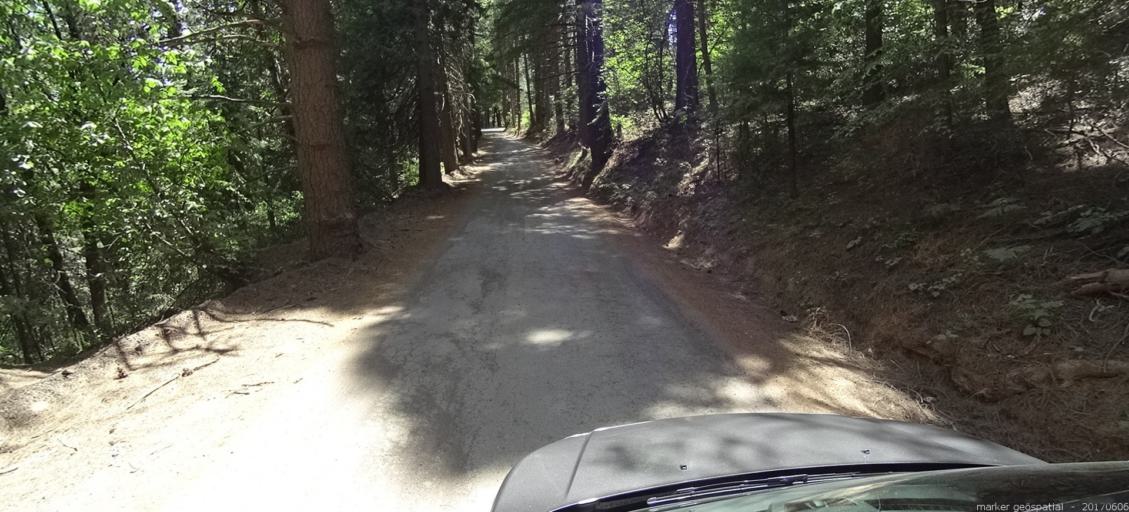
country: US
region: California
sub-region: Siskiyou County
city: Mount Shasta
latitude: 41.2737
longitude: -122.2864
